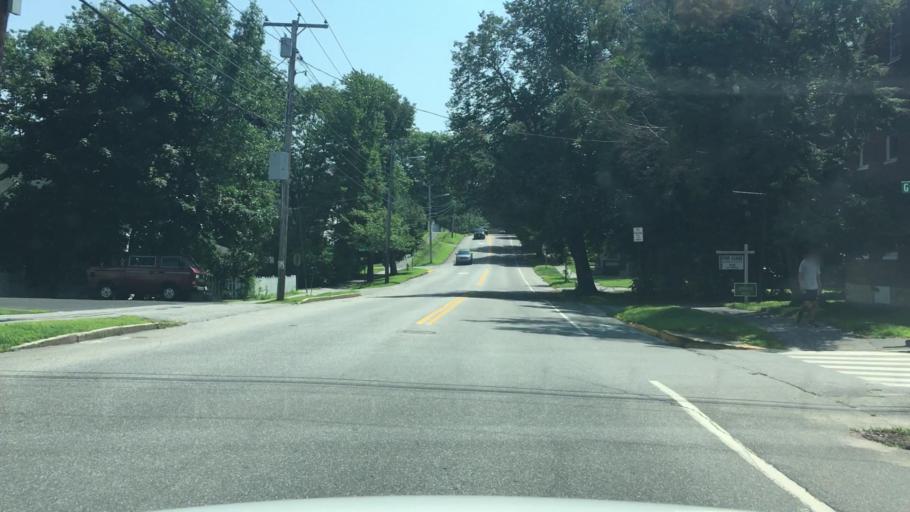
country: US
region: Maine
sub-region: Cumberland County
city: Brunswick
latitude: 43.9141
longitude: -69.9621
